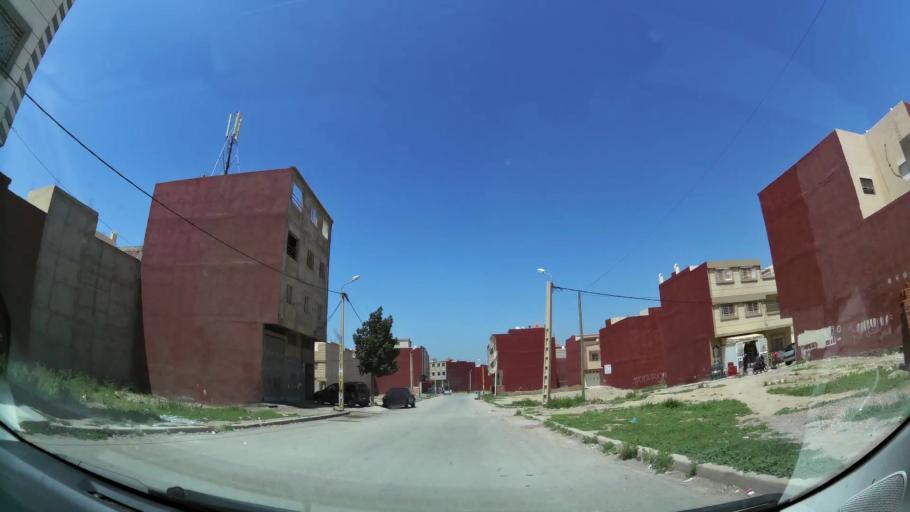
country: MA
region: Oriental
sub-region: Oujda-Angad
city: Oujda
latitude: 34.6972
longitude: -1.8870
